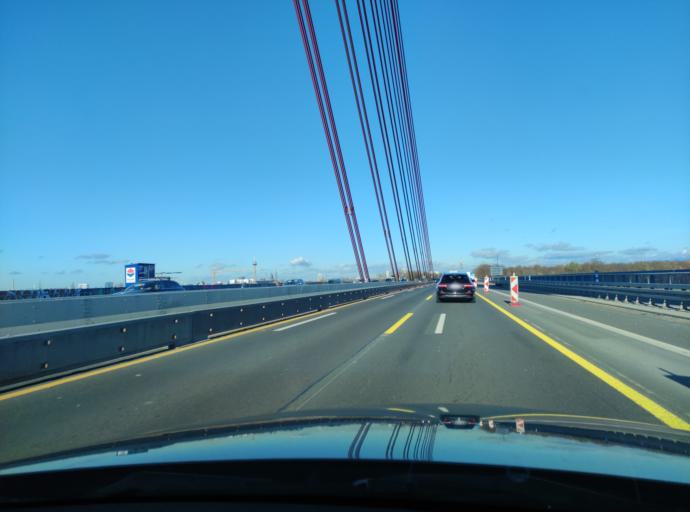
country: DE
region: North Rhine-Westphalia
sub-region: Regierungsbezirk Dusseldorf
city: Dusseldorf
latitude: 51.1839
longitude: 6.7752
